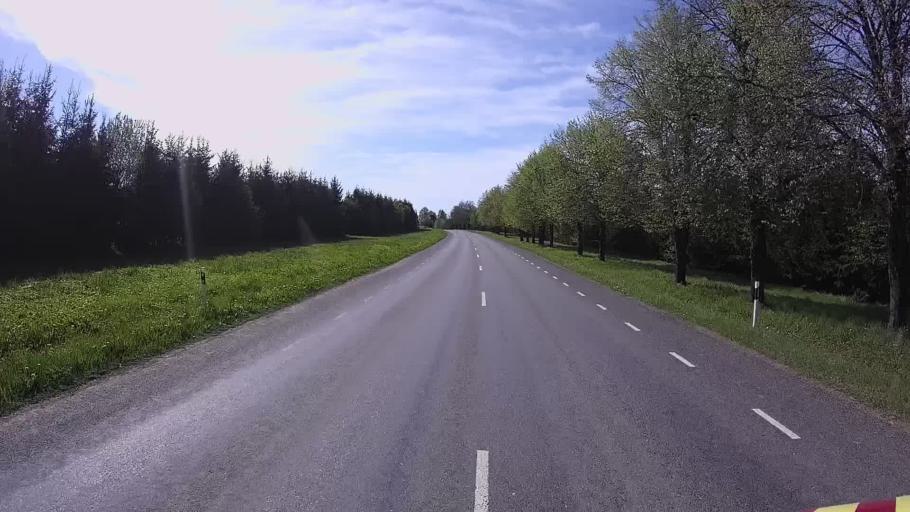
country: EE
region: Polvamaa
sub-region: Polva linn
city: Polva
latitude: 58.1942
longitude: 27.0803
